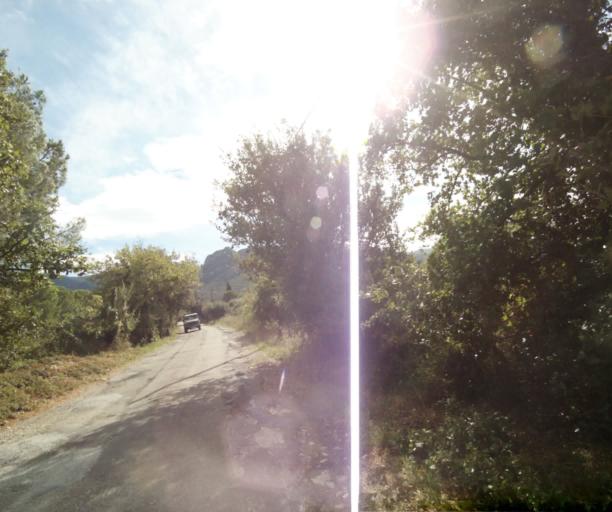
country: FR
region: Languedoc-Roussillon
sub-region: Departement des Pyrenees-Orientales
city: Sant Andreu de Sureda
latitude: 42.5358
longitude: 2.9859
